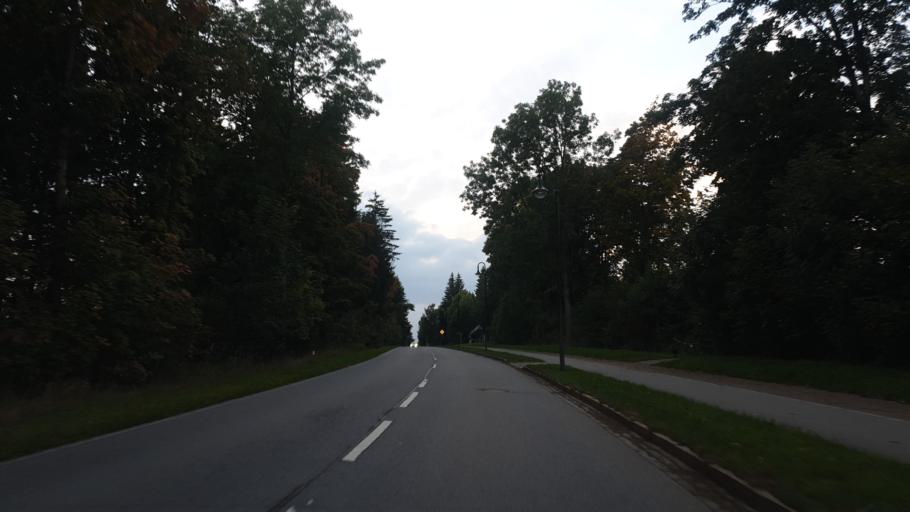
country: DE
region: Saxony
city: Johanngeorgenstadt
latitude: 50.4389
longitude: 12.7034
